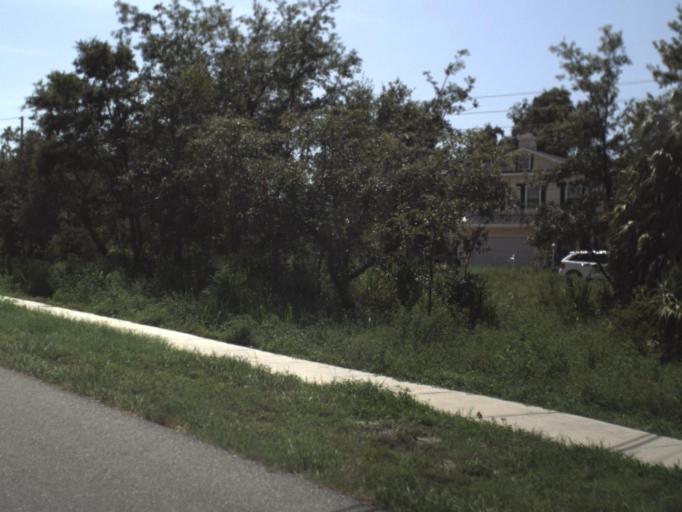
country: US
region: Florida
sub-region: Pinellas County
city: Palm Harbor
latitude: 28.1009
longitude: -82.7723
